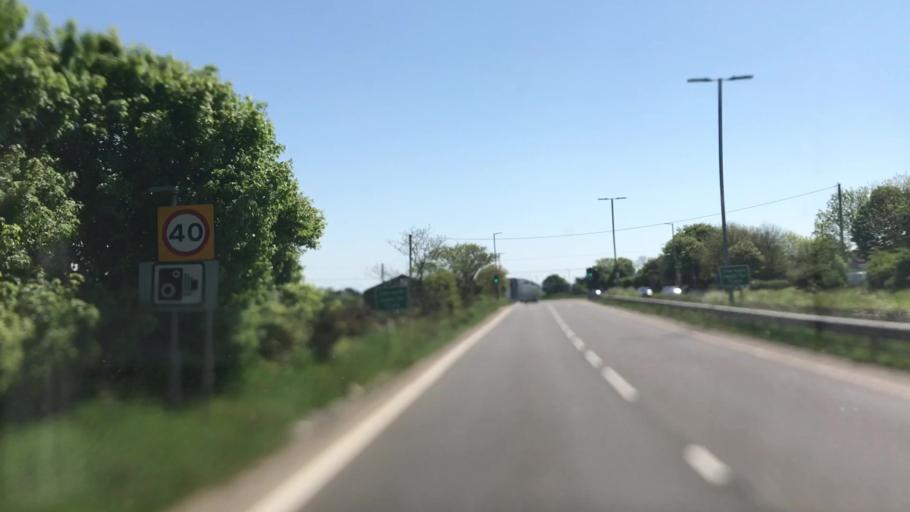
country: GB
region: England
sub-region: Cornwall
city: Truro
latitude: 50.2642
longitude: -5.1107
